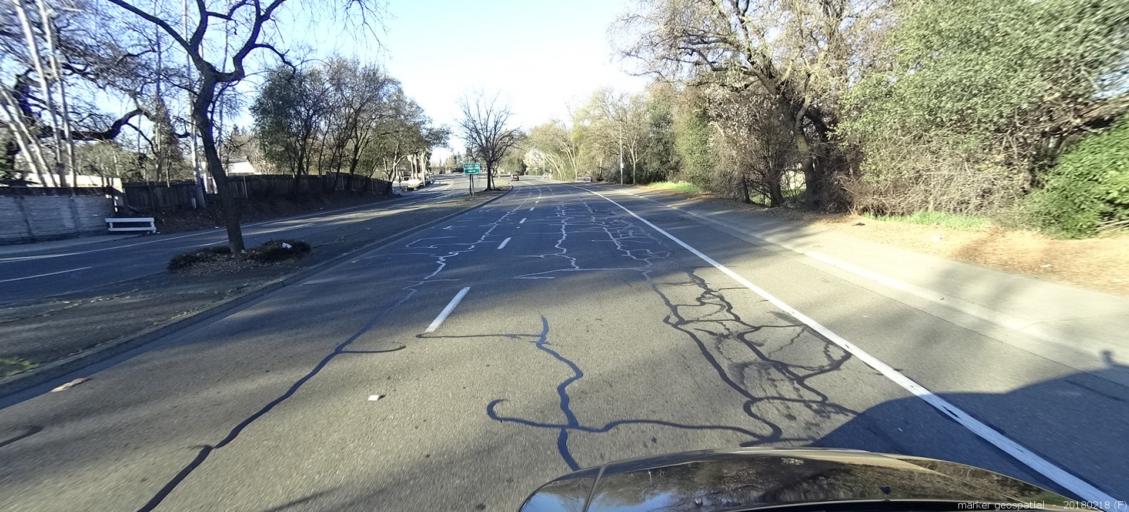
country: US
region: California
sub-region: Sacramento County
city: Orangevale
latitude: 38.6712
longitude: -121.2052
